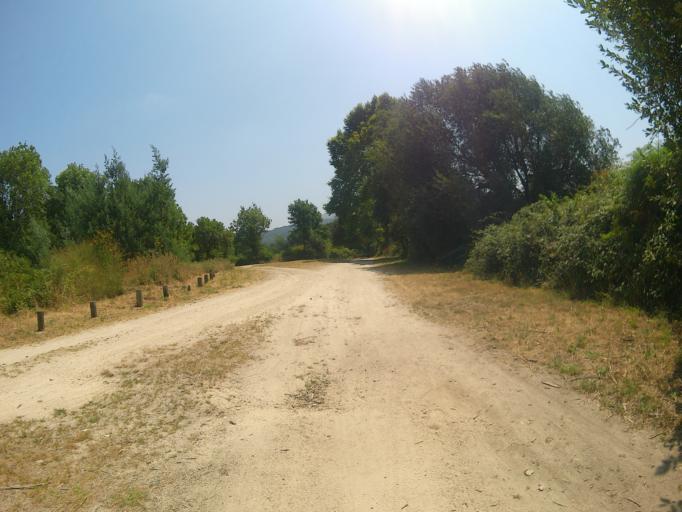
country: PT
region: Viana do Castelo
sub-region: Ponte de Lima
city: Ponte de Lima
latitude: 41.7764
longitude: -8.5713
